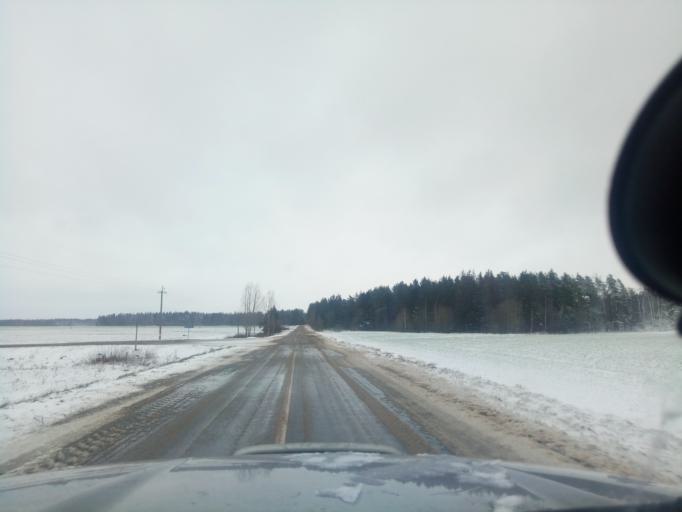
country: BY
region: Minsk
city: Tsimkavichy
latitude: 53.0481
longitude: 26.8664
